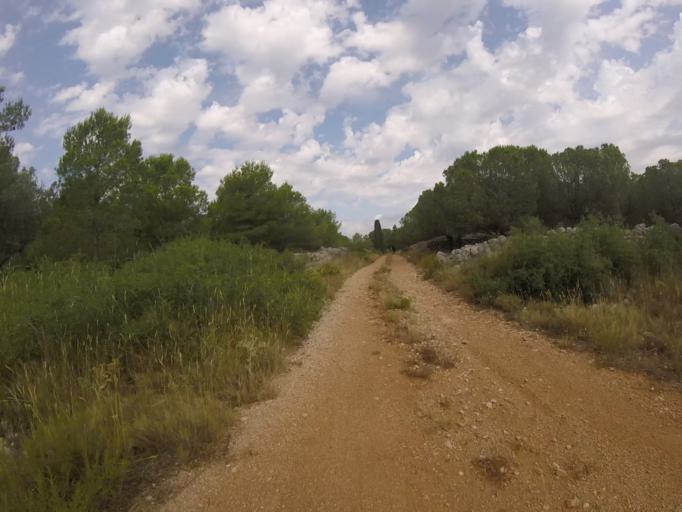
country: ES
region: Valencia
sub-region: Provincia de Castello
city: Alcala de Xivert
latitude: 40.3634
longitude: 0.1965
